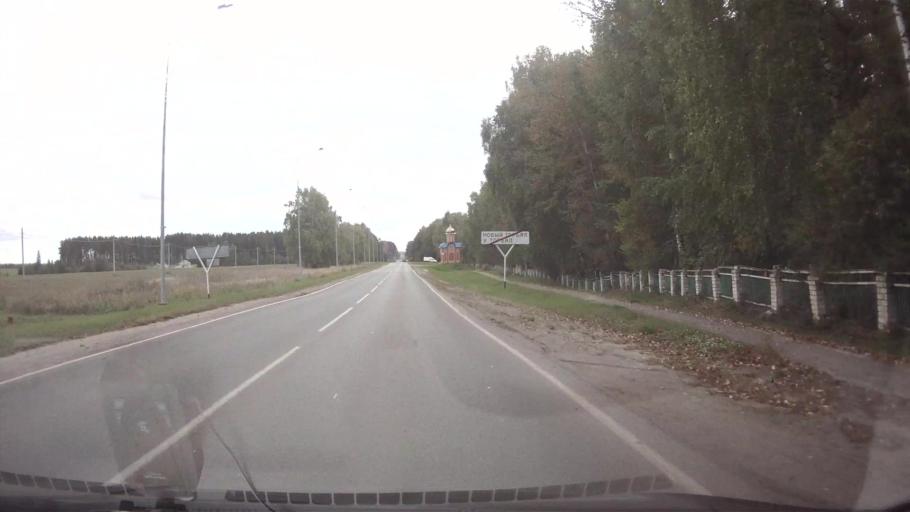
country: RU
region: Mariy-El
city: Kuzhener
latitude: 56.9950
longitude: 48.7425
